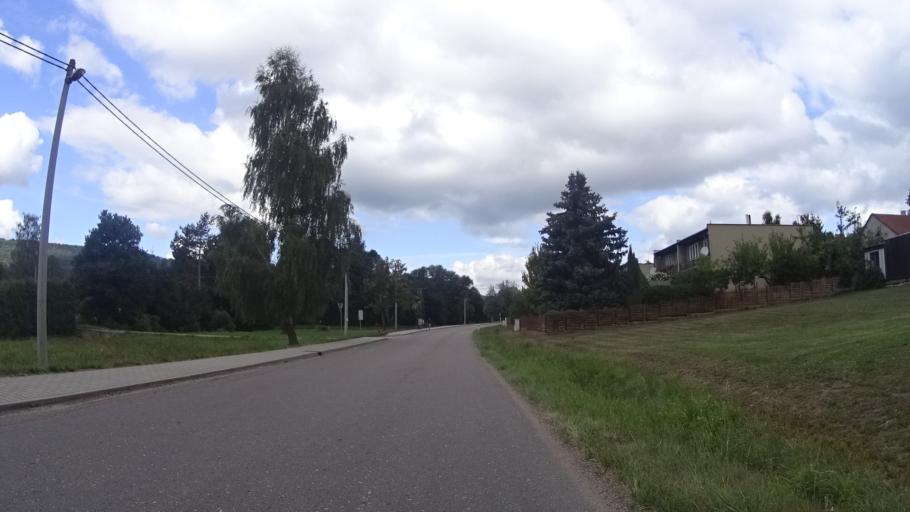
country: CZ
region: Pardubicky
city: Dolni Cermna
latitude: 49.9309
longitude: 16.5392
